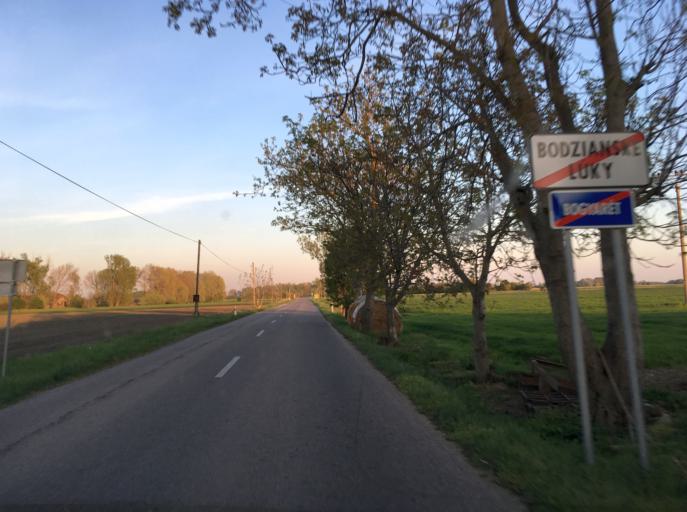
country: SK
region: Nitriansky
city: Kolarovo
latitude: 47.8867
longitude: 17.8990
